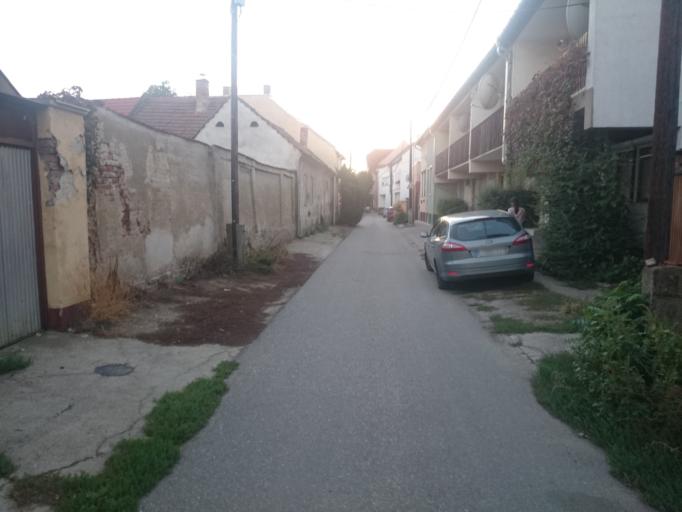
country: HU
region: Hajdu-Bihar
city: Debrecen
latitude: 47.5314
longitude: 21.6157
